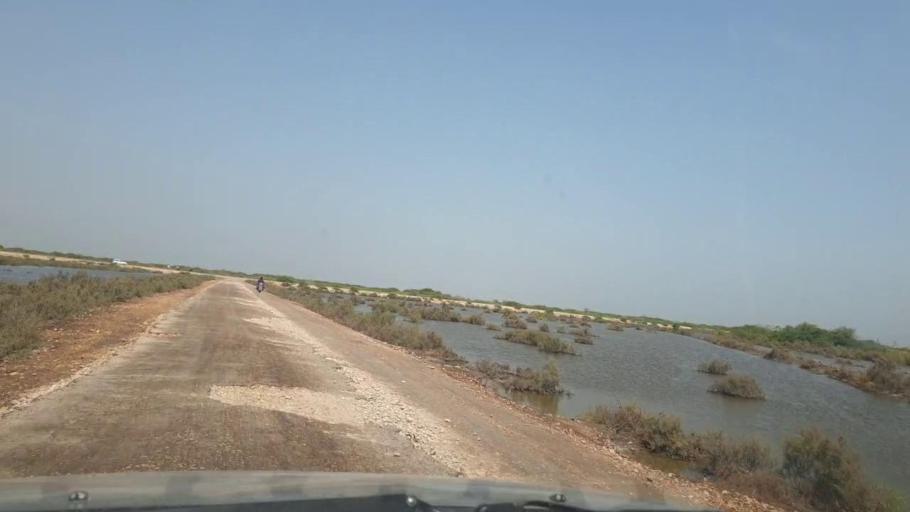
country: PK
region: Sindh
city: Tando Ghulam Ali
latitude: 25.1126
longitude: 68.8021
